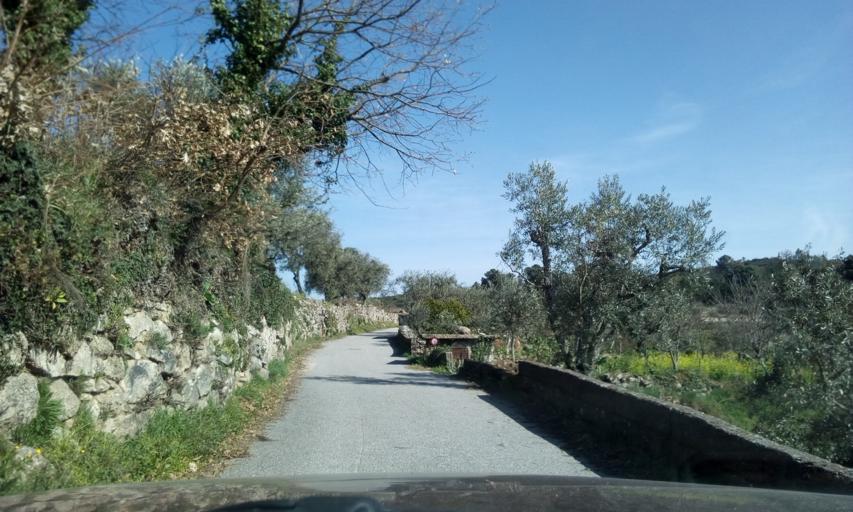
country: PT
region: Guarda
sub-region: Celorico da Beira
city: Celorico da Beira
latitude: 40.6551
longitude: -7.4087
